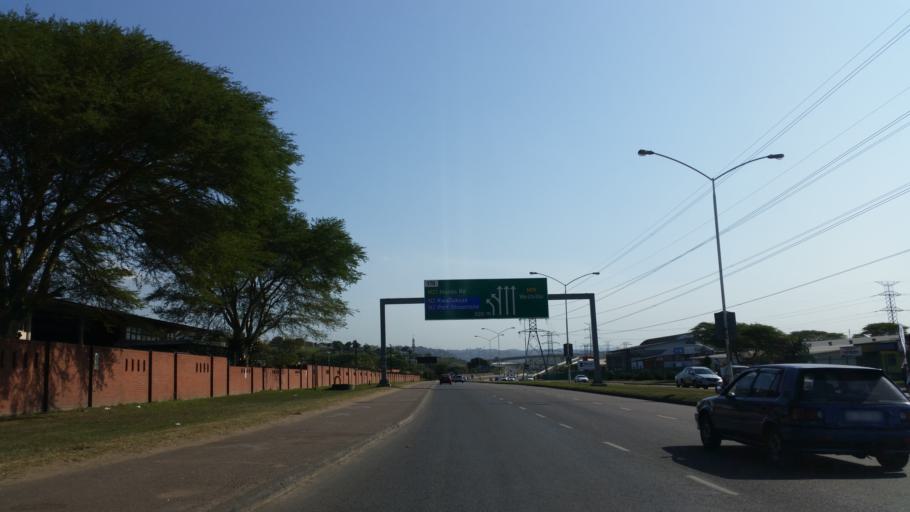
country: ZA
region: KwaZulu-Natal
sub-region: eThekwini Metropolitan Municipality
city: Berea
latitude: -29.8111
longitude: 30.9879
